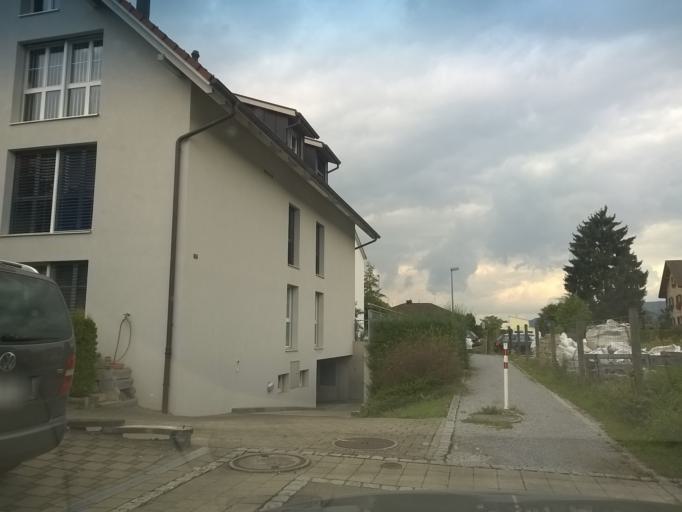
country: CH
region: Zurich
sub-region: Bezirk Buelach
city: Embrach / Embrach (Dorfkern)
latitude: 47.5009
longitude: 8.5996
